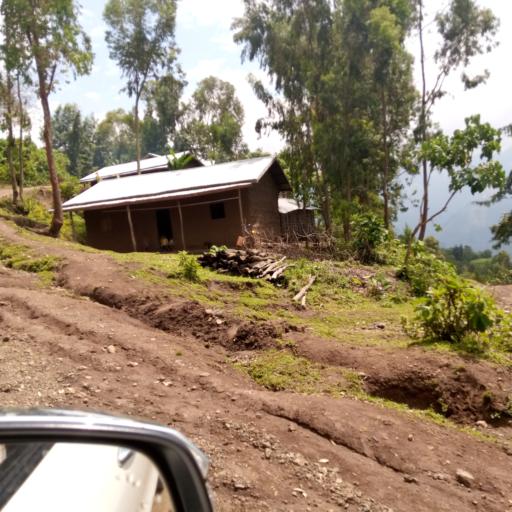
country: ET
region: Southern Nations, Nationalities, and People's Region
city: Arba Minch'
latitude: 6.3125
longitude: 37.3707
